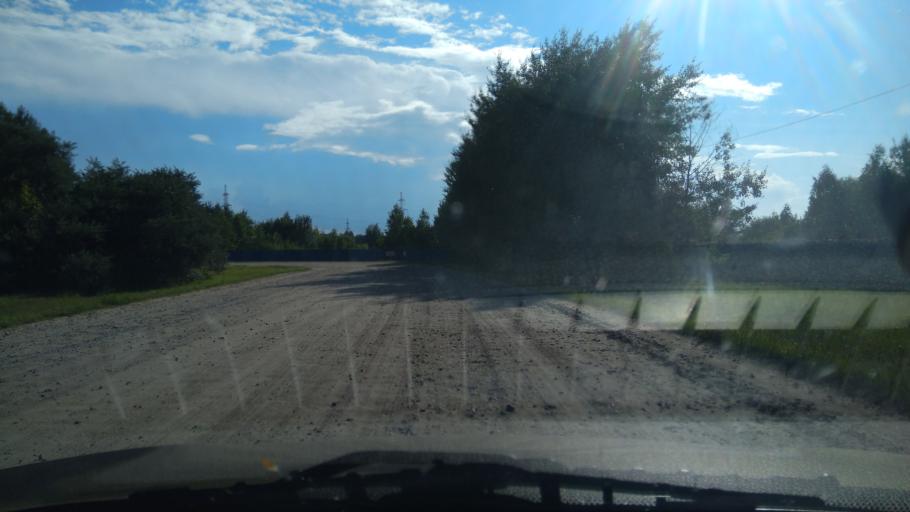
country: BY
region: Brest
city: Byelaazyorsk
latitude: 52.4571
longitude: 25.1876
